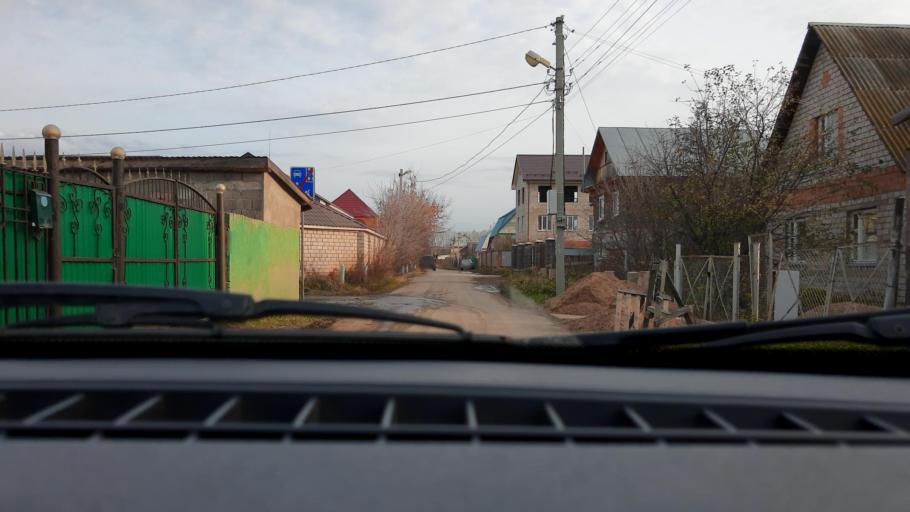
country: RU
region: Bashkortostan
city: Mikhaylovka
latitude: 54.7830
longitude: 55.8973
